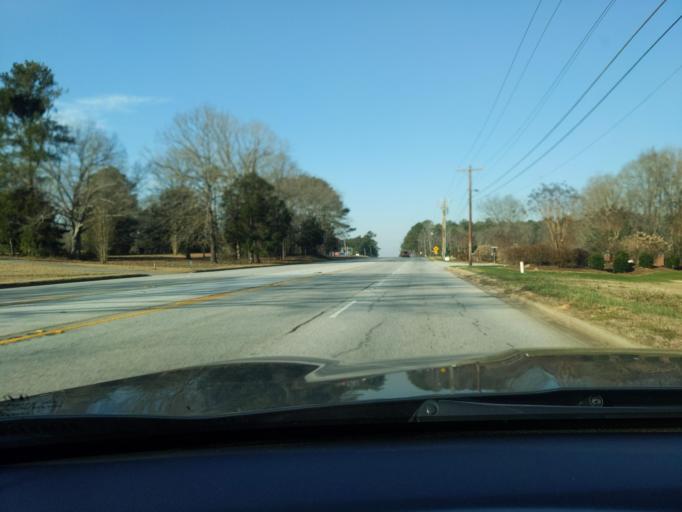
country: US
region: South Carolina
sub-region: Greenwood County
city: Greenwood
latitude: 34.1904
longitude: -82.2361
